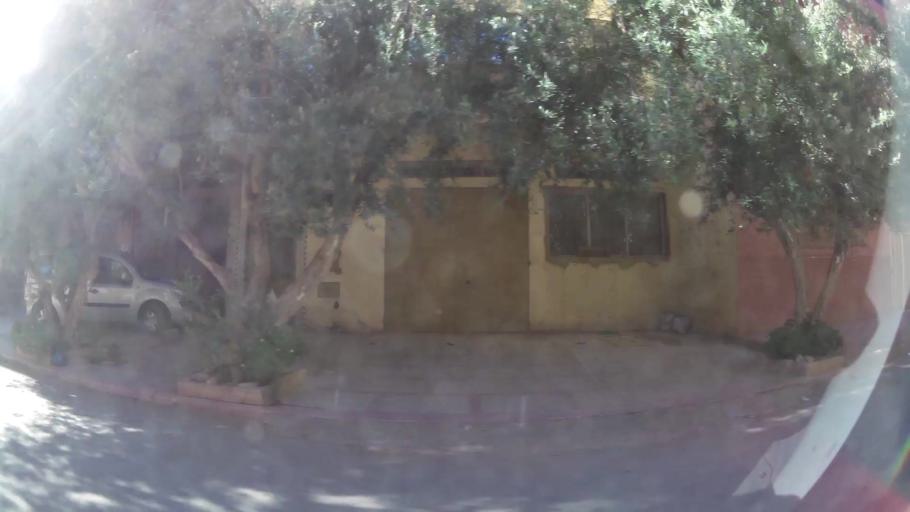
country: MA
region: Oriental
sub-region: Berkane-Taourirt
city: Berkane
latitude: 34.9327
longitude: -2.3322
